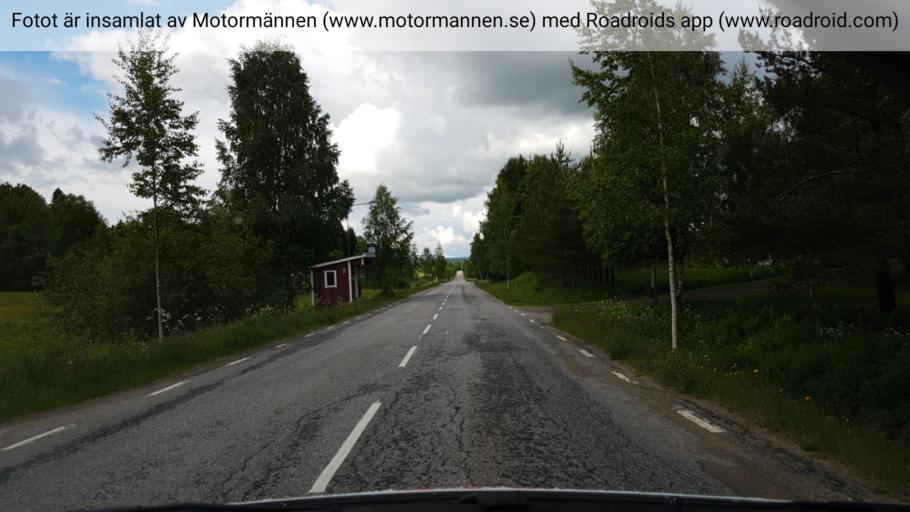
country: SE
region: Vaesterbotten
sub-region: Vannas Kommun
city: Vannasby
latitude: 63.8770
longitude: 19.8927
